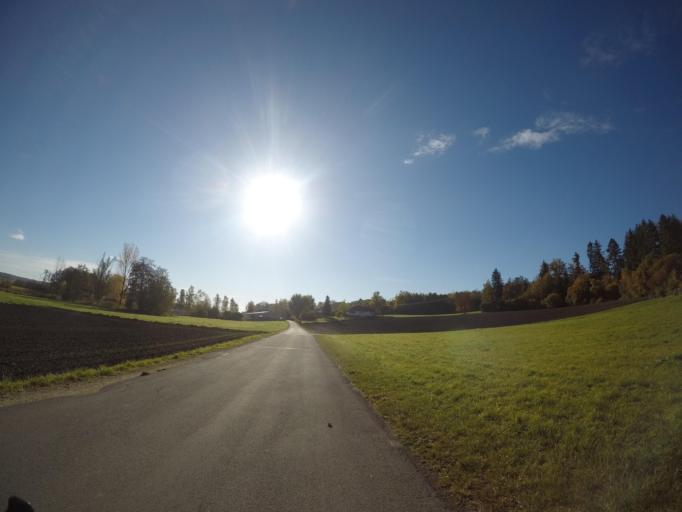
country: DE
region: Baden-Wuerttemberg
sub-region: Tuebingen Region
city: Saulgau
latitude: 48.0346
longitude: 9.4753
